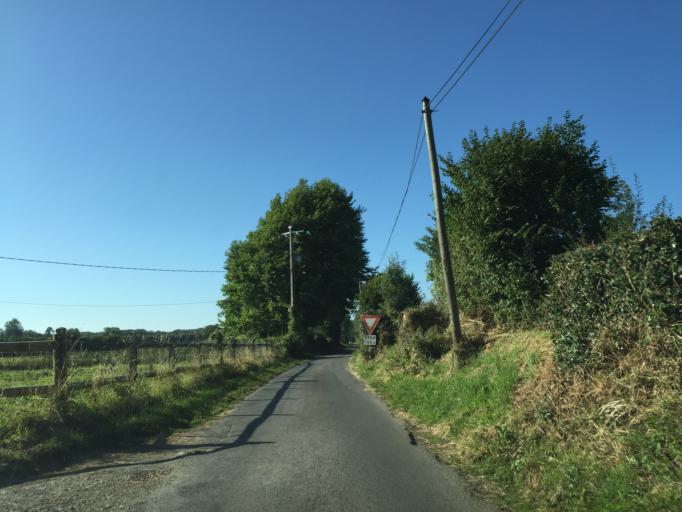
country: FR
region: Lower Normandy
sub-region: Departement du Calvados
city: Equemauville
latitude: 49.3958
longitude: 0.1996
